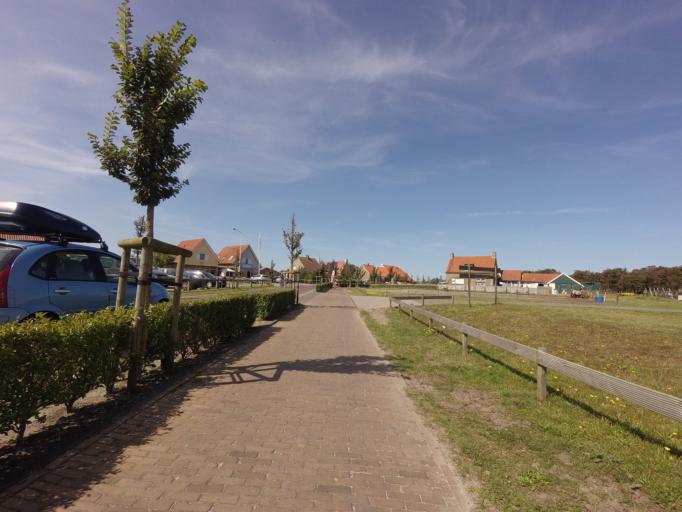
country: NL
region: Friesland
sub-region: Gemeente Ameland
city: Hollum
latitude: 53.4432
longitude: 5.6358
